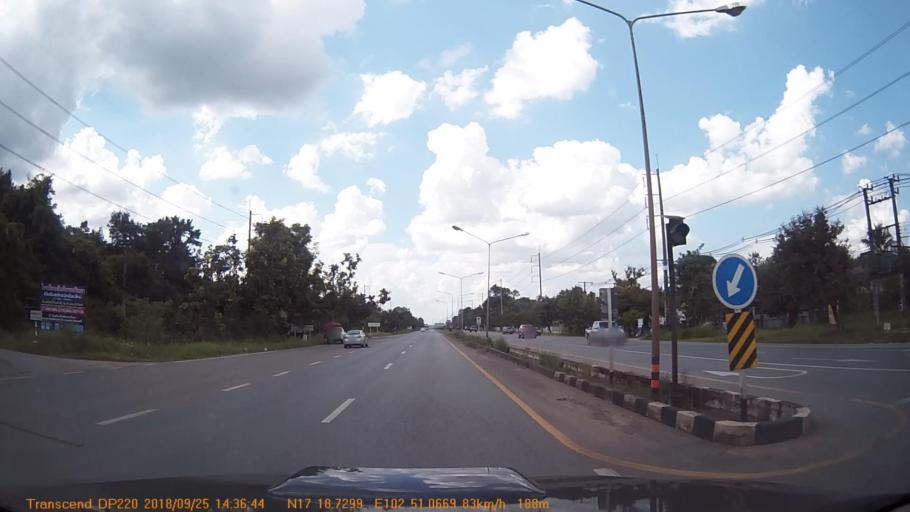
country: TH
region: Changwat Udon Thani
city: Udon Thani
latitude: 17.3124
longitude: 102.8510
